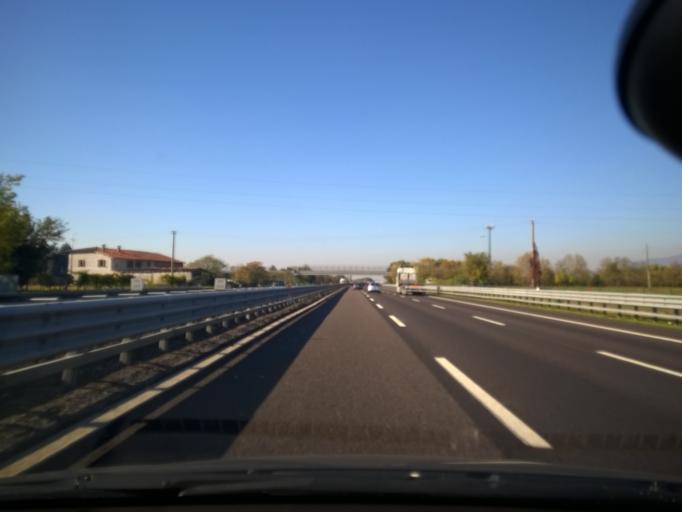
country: IT
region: Lombardy
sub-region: Provincia di Brescia
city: Calcinato
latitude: 45.4681
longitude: 10.3857
